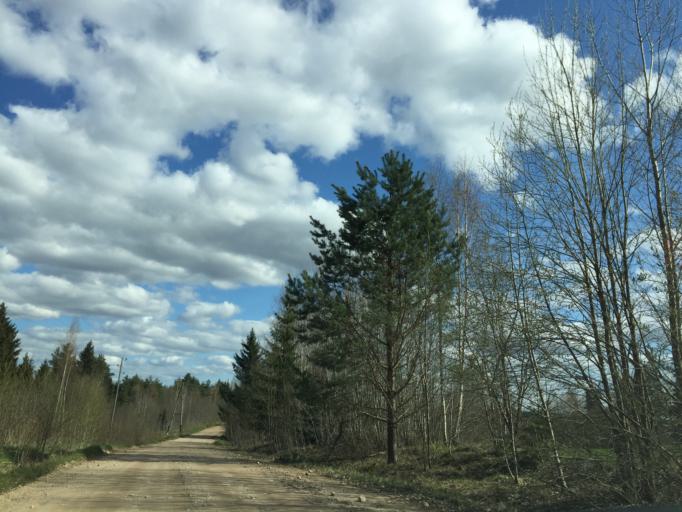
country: LV
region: Rezekne
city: Rezekne
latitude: 56.6546
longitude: 27.2816
